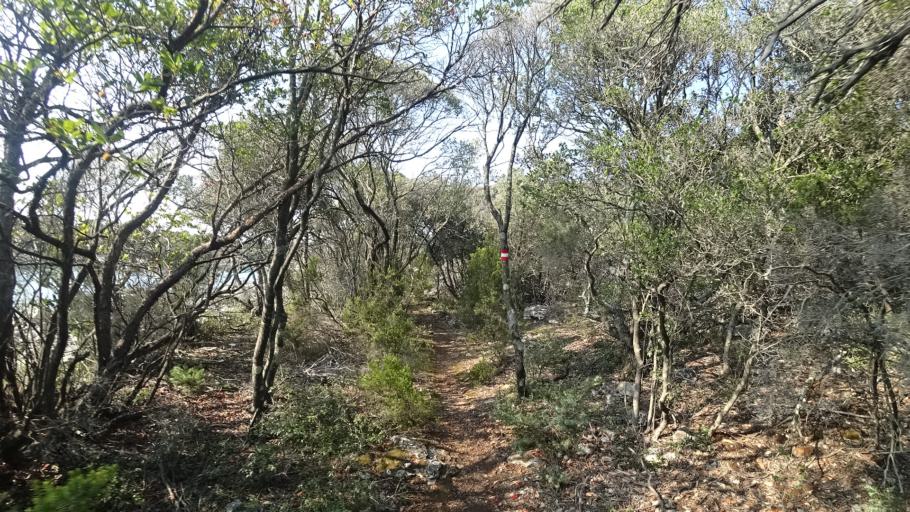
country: HR
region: Primorsko-Goranska
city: Mali Losinj
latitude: 44.4874
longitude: 14.5087
